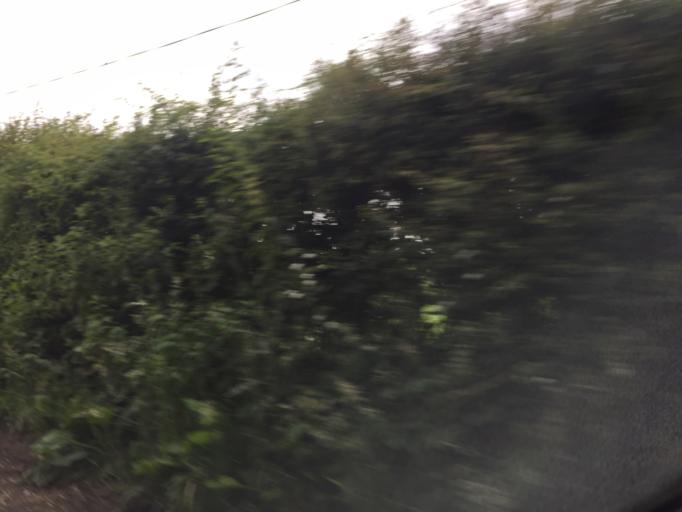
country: GB
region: England
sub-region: South Gloucestershire
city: Horton
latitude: 51.5646
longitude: -2.3535
